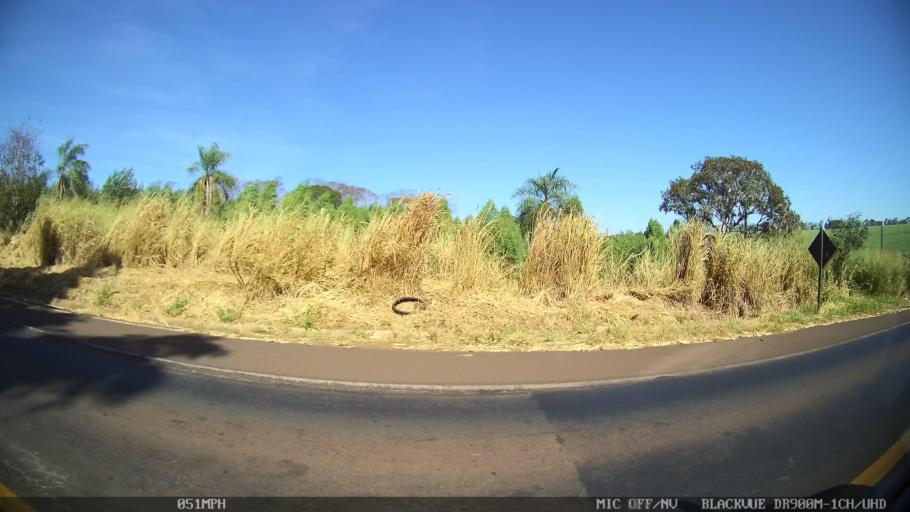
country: BR
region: Sao Paulo
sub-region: Barretos
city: Barretos
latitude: -20.6073
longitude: -48.7437
